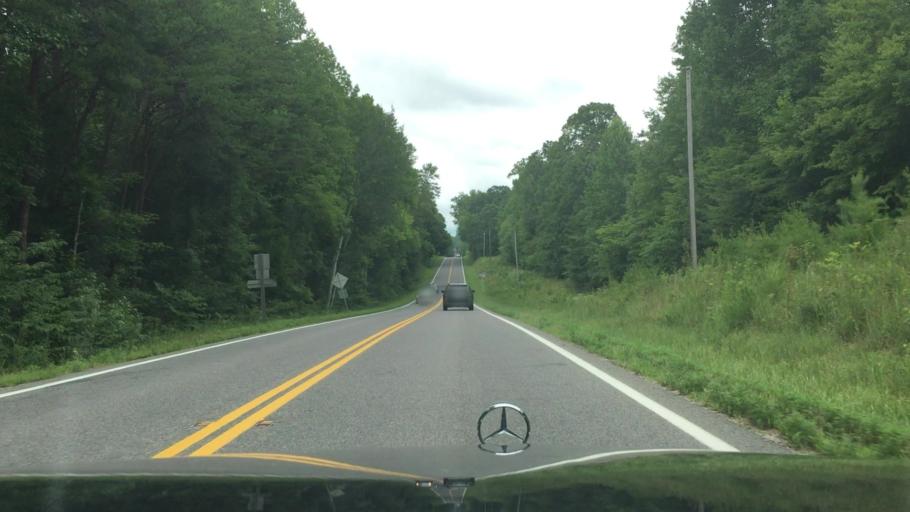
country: US
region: Virginia
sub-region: Nottoway County
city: Crewe
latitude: 37.2790
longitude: -78.1889
